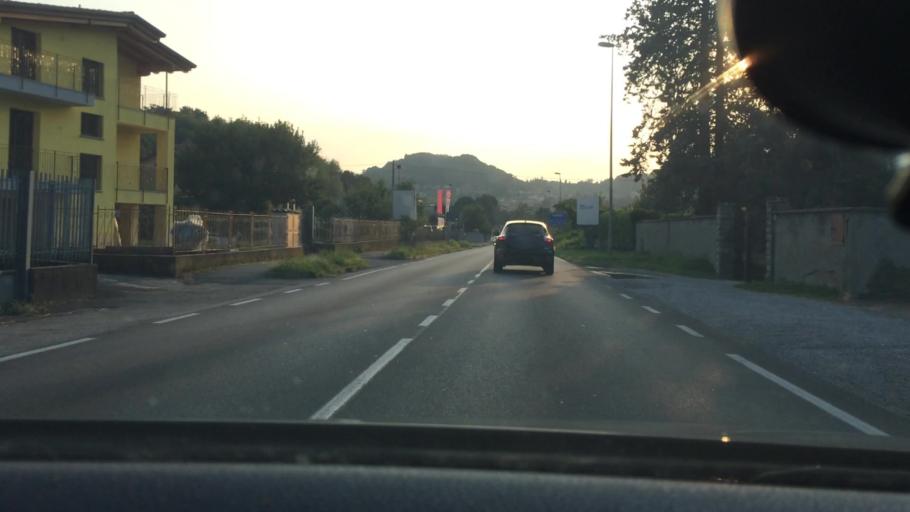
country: IT
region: Lombardy
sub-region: Provincia di Lecco
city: Calco
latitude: 45.7347
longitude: 9.4234
